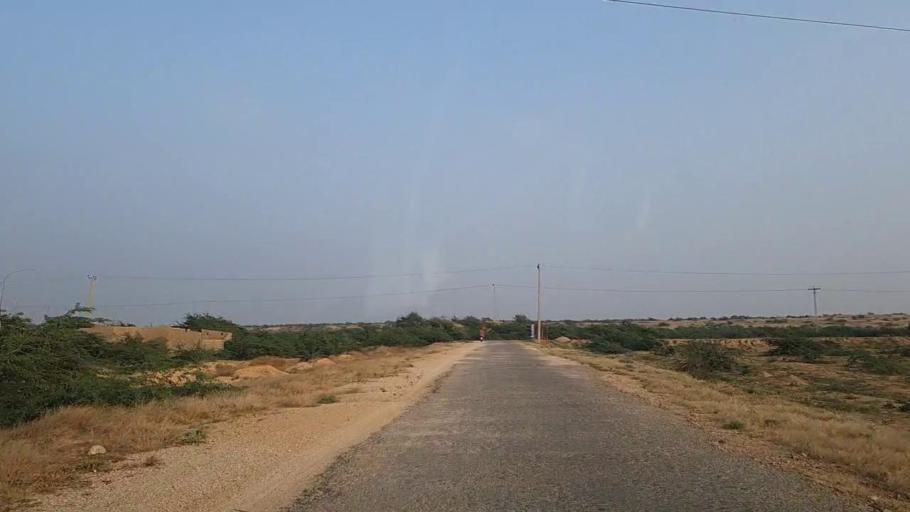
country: PK
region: Sindh
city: Thatta
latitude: 24.6884
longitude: 67.8519
